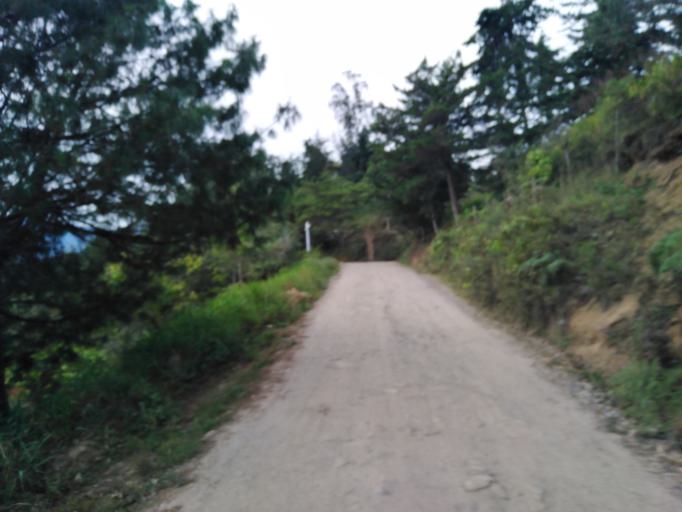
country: CO
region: Cundinamarca
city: Tenza
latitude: 5.1003
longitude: -73.4167
